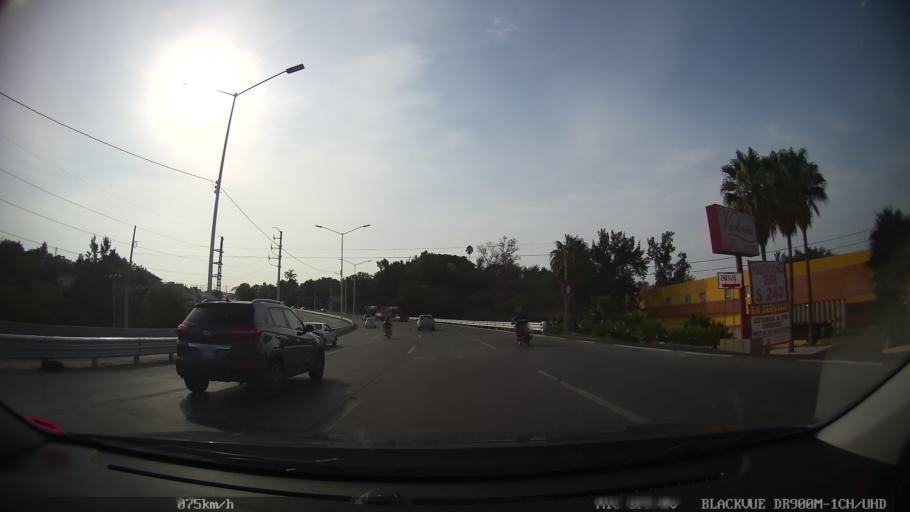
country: MX
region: Jalisco
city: Tlaquepaque
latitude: 20.6841
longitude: -103.2539
